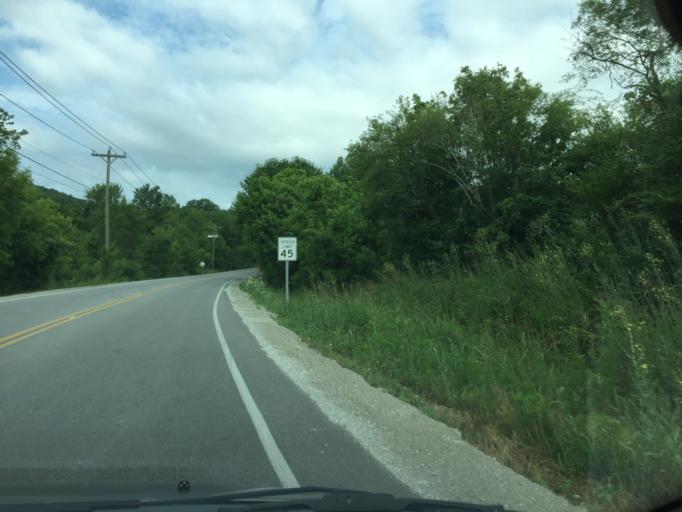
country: US
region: Tennessee
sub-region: Hamilton County
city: Apison
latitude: 34.9880
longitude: -85.0650
